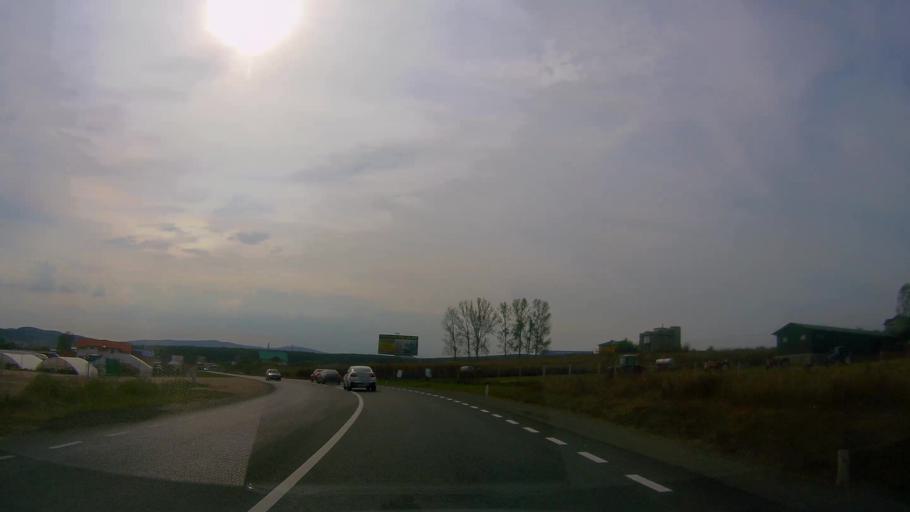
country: RO
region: Salaj
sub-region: Comuna Hereclean
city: Hereclean
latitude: 47.2303
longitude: 22.9984
